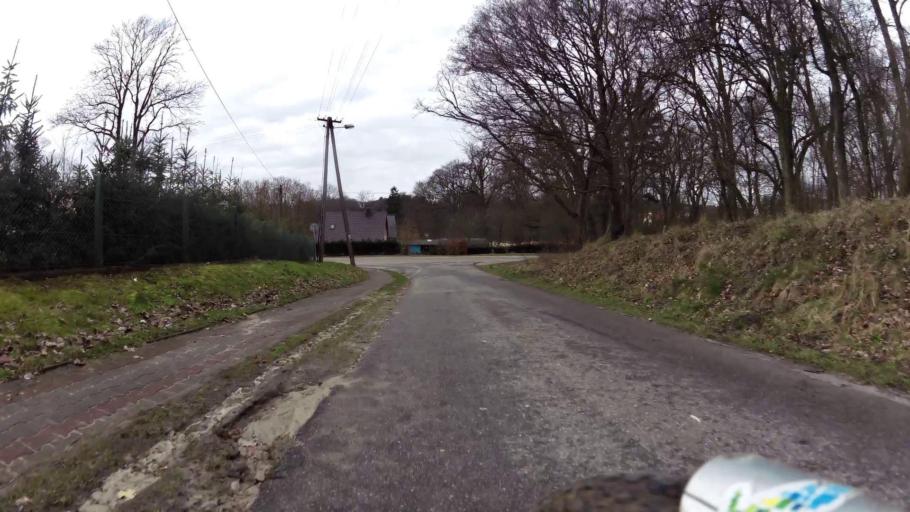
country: PL
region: Pomeranian Voivodeship
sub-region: Powiat bytowski
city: Kolczyglowy
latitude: 54.2403
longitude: 17.2434
